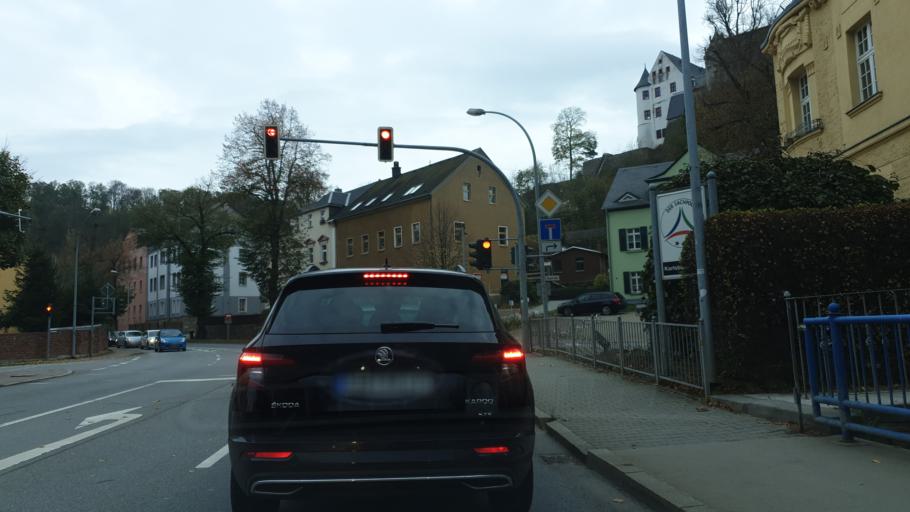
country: DE
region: Saxony
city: Schwarzenberg
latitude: 50.5387
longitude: 12.7879
